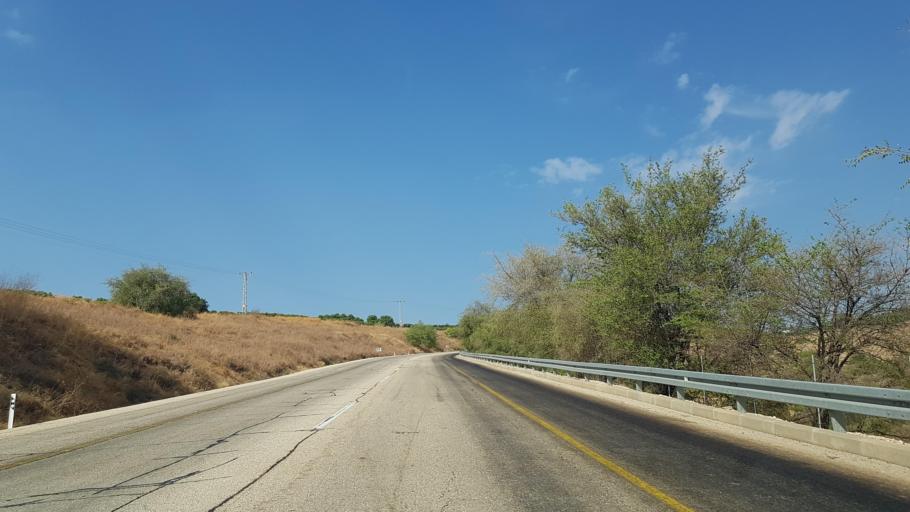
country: SY
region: Quneitra
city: Al Butayhah
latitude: 32.8974
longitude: 35.5970
